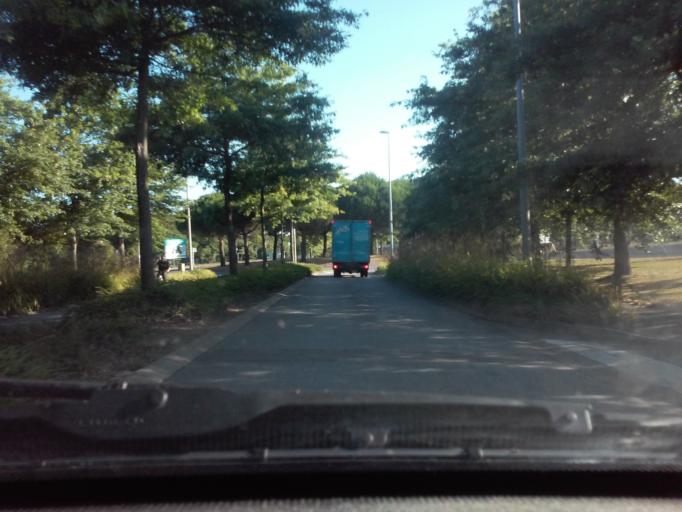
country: FR
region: Pays de la Loire
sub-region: Departement de la Loire-Atlantique
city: Saint-Andre-des-Eaux
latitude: 47.2943
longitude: -2.2884
